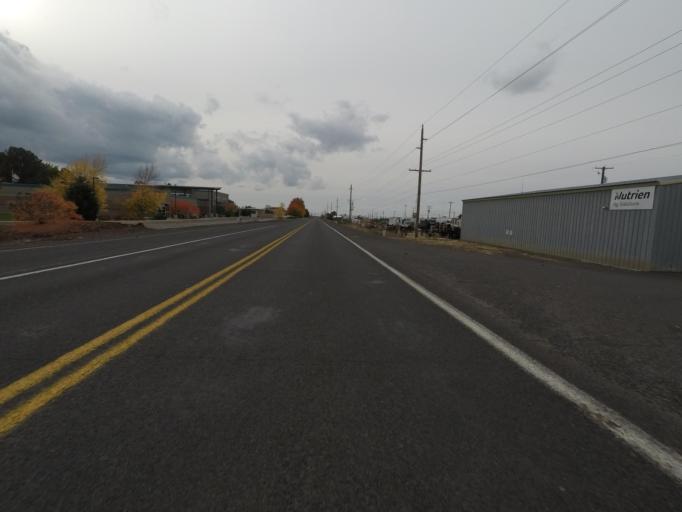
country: US
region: Washington
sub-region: Walla Walla County
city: Walla Walla East
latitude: 46.0814
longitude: -118.2785
